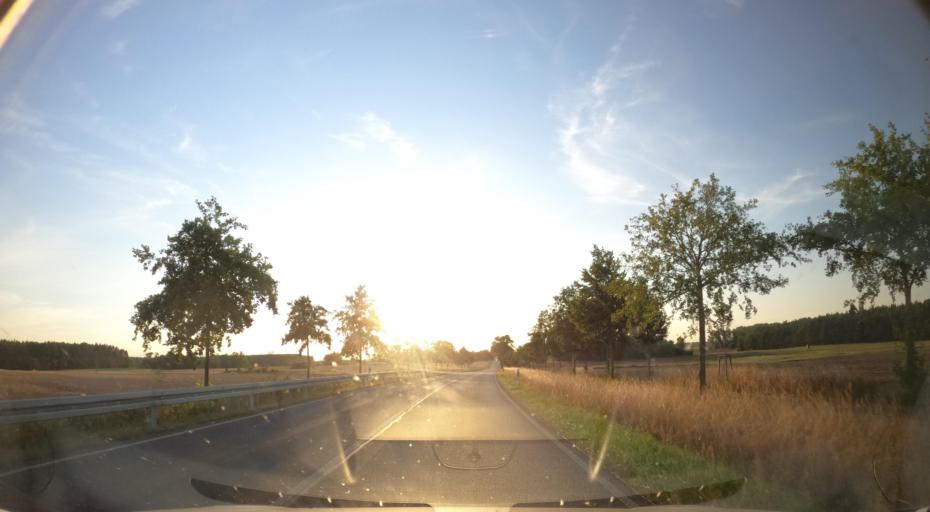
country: DE
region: Mecklenburg-Vorpommern
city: Viereck
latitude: 53.4999
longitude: 14.0501
